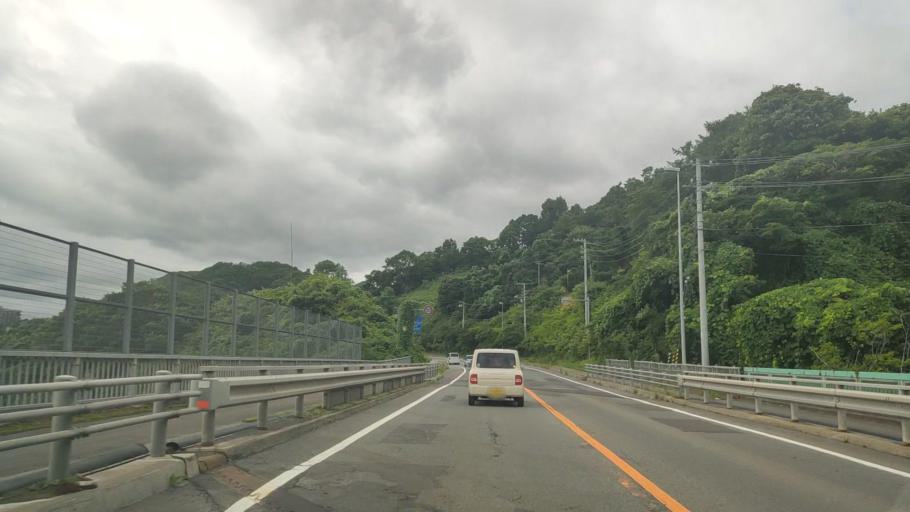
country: JP
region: Hokkaido
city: Date
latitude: 42.5544
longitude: 140.7547
